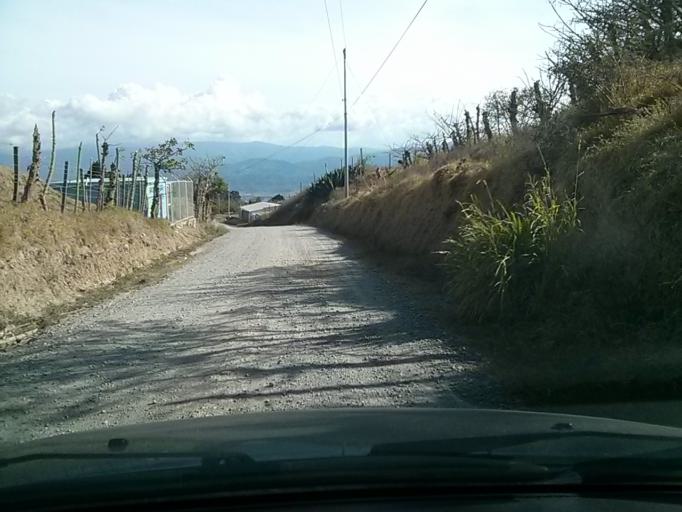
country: CR
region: Cartago
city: Cot
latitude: 9.9091
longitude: -83.9126
